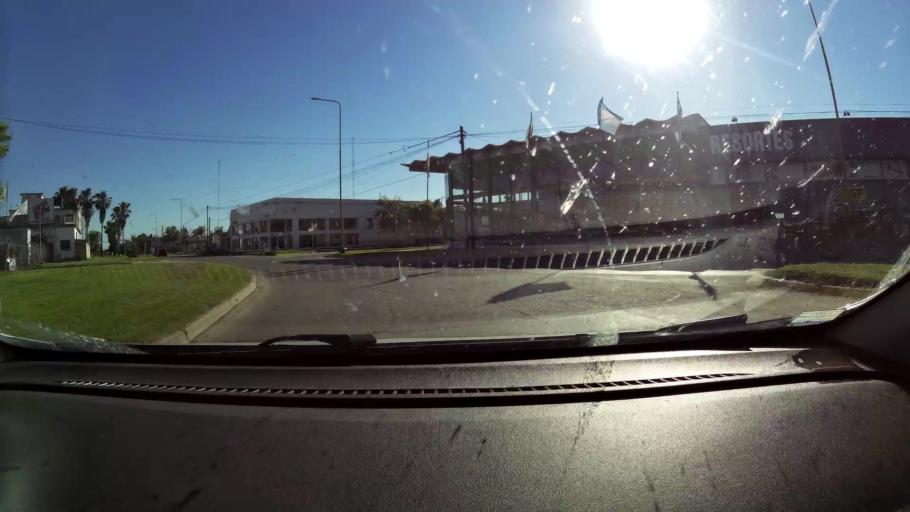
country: AR
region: Cordoba
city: San Francisco
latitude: -31.4145
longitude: -62.0939
